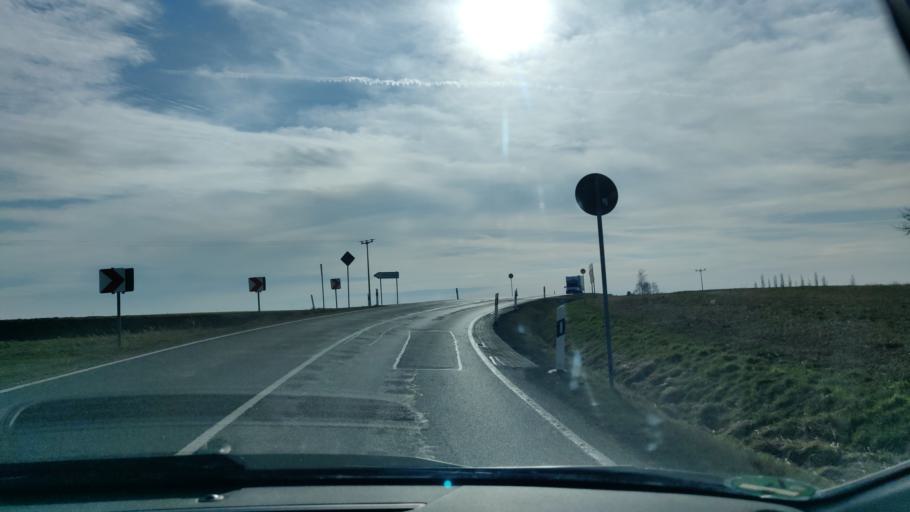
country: DE
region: Saxony
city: Wechselburg
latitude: 51.0254
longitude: 12.7509
